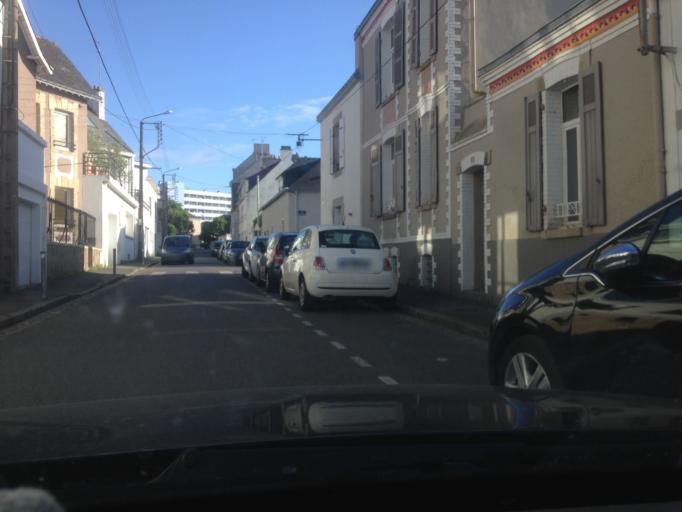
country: FR
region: Brittany
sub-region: Departement du Morbihan
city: Lorient
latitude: 47.7434
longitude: -3.3730
